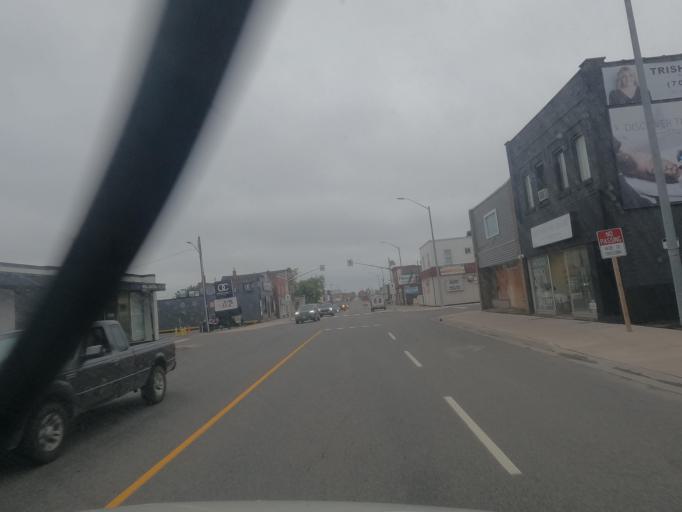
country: CA
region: Ontario
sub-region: Algoma
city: Sault Ste. Marie
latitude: 46.5259
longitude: -84.3470
